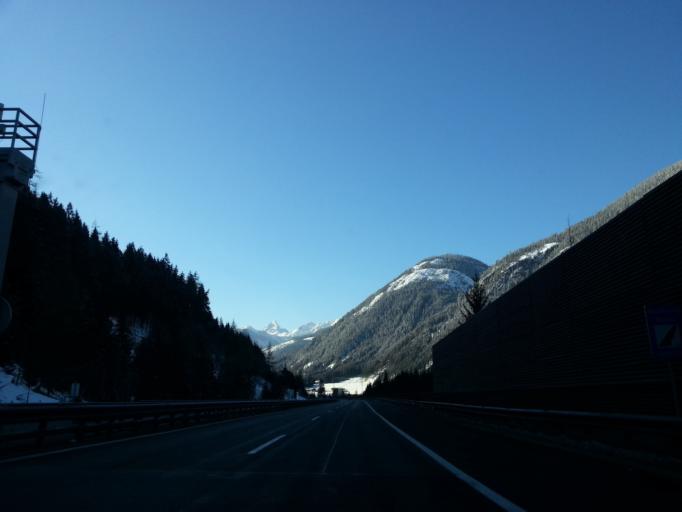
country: AT
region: Salzburg
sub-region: Politischer Bezirk Sankt Johann im Pongau
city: Flachau
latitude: 47.3390
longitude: 13.3951
